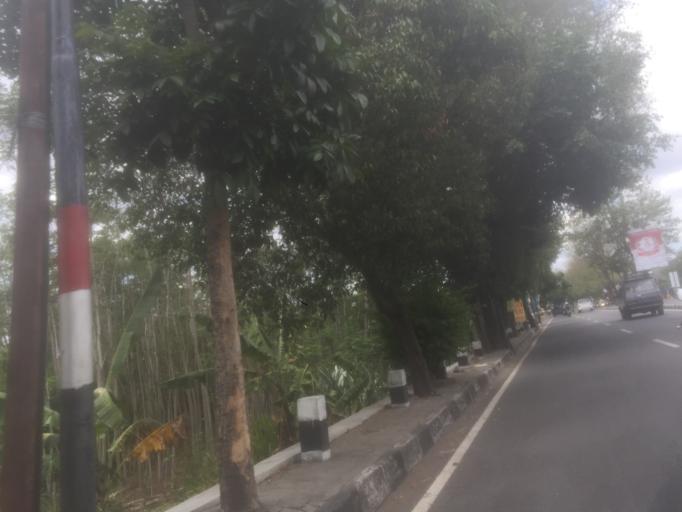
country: ID
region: Daerah Istimewa Yogyakarta
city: Melati
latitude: -7.7271
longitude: 110.3630
